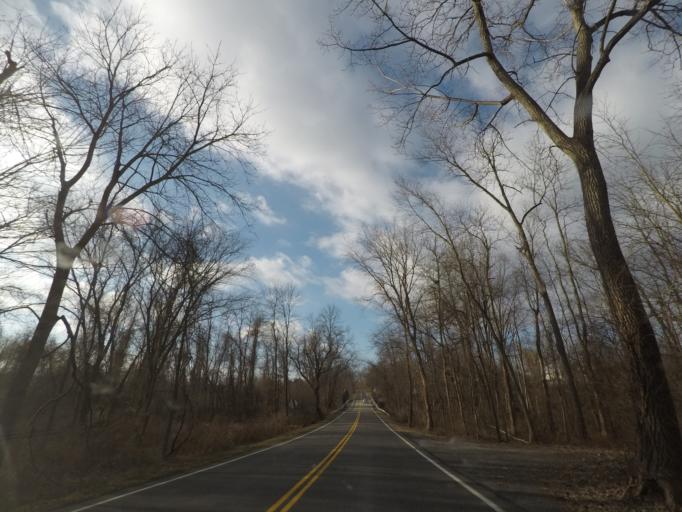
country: US
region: New York
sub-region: Albany County
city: Westmere
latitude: 42.6635
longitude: -73.8810
